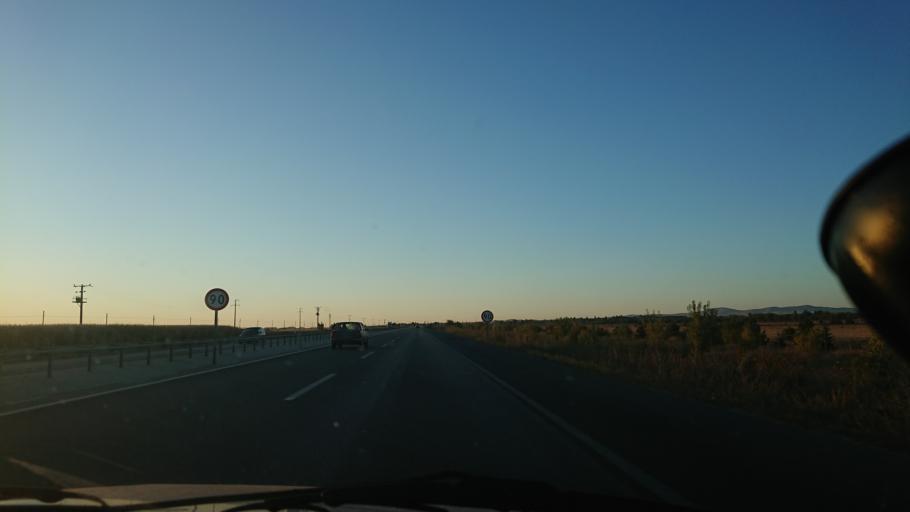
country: TR
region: Eskisehir
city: Mahmudiye
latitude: 39.5489
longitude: 30.9290
